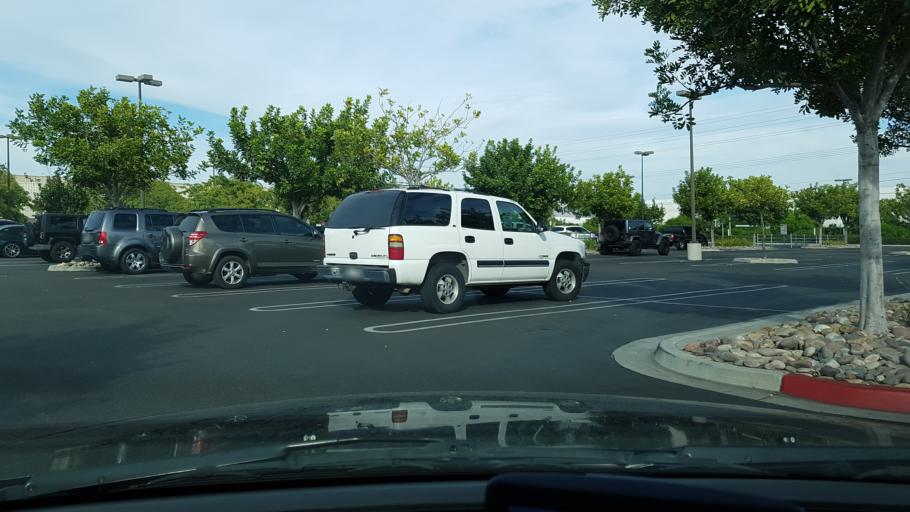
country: US
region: California
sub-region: San Diego County
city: Poway
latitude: 32.9354
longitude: -117.0334
